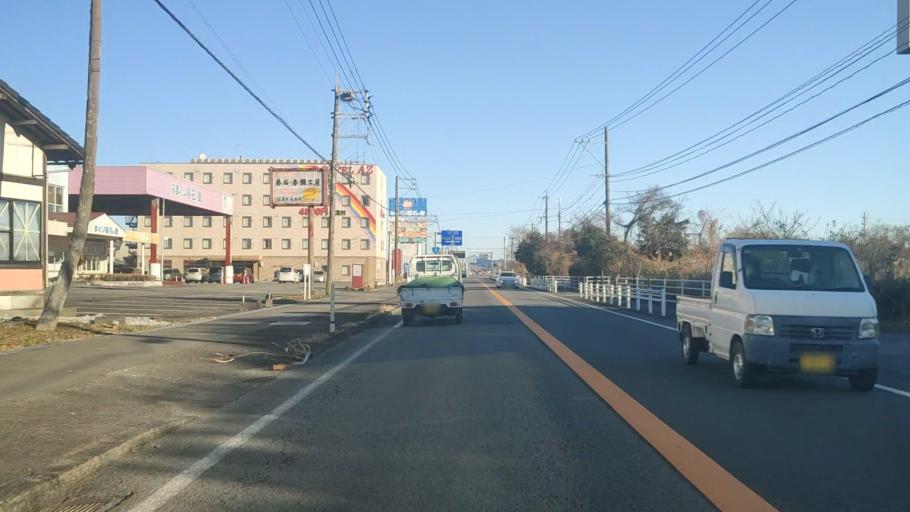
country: JP
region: Miyazaki
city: Nobeoka
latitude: 32.3931
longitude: 131.6283
